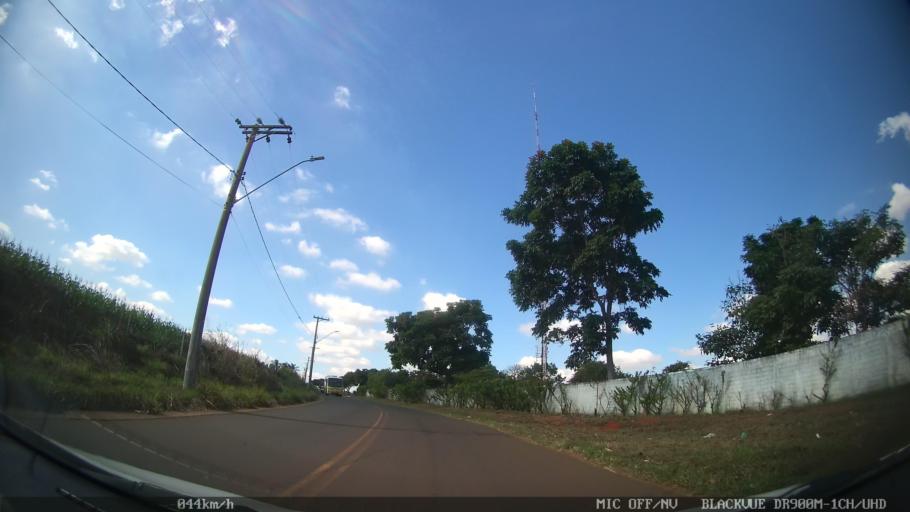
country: BR
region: Sao Paulo
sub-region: Hortolandia
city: Hortolandia
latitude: -22.8767
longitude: -47.2491
